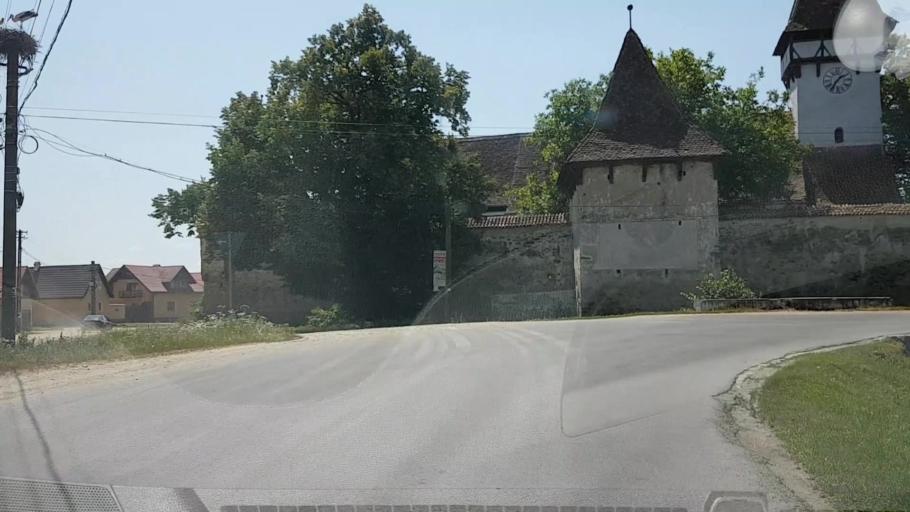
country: RO
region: Brasov
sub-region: Comuna Voila
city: Voila
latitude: 45.8370
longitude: 24.8345
